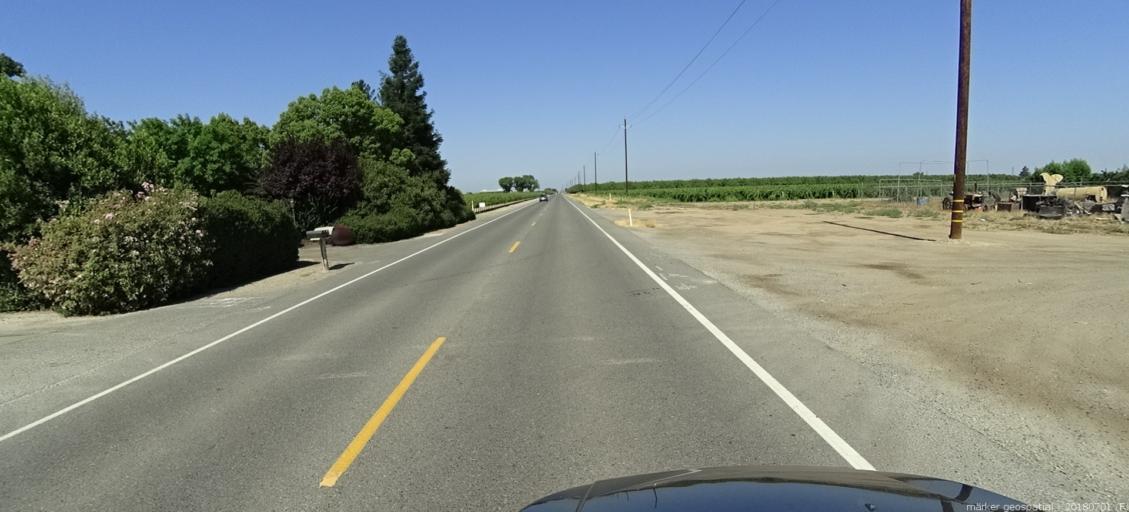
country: US
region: California
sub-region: Madera County
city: Bonadelle Ranchos-Madera Ranchos
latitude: 36.8803
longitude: -119.9250
